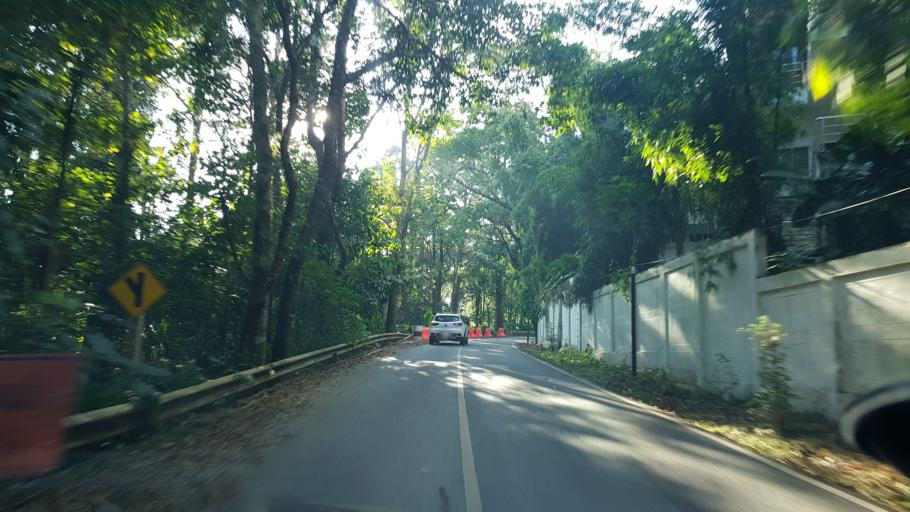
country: TH
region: Chiang Rai
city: Mae Fa Luang
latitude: 20.3273
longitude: 99.8263
